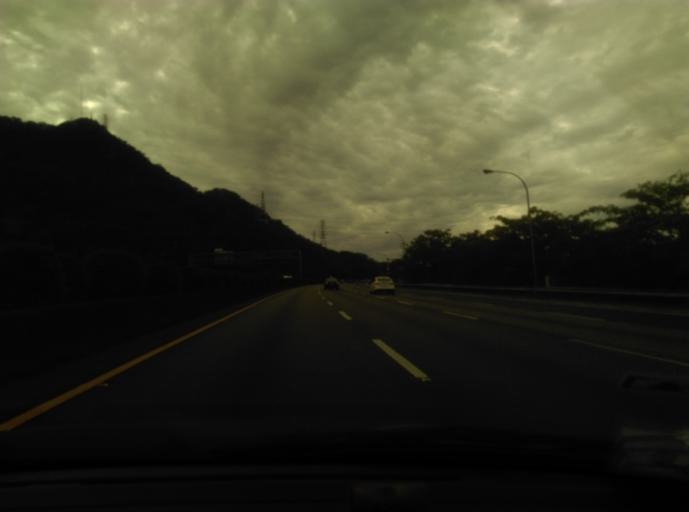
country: TW
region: Taiwan
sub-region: Taoyuan
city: Taoyuan
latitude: 24.9378
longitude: 121.3586
